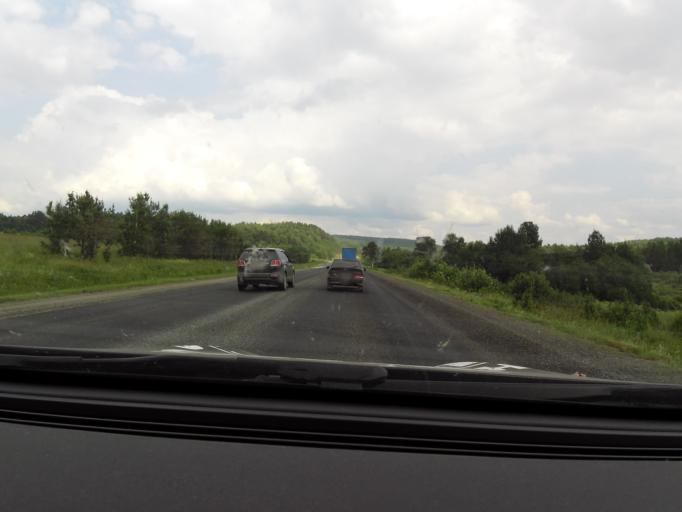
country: RU
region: Sverdlovsk
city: Ufimskiy
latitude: 56.7709
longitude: 58.2089
